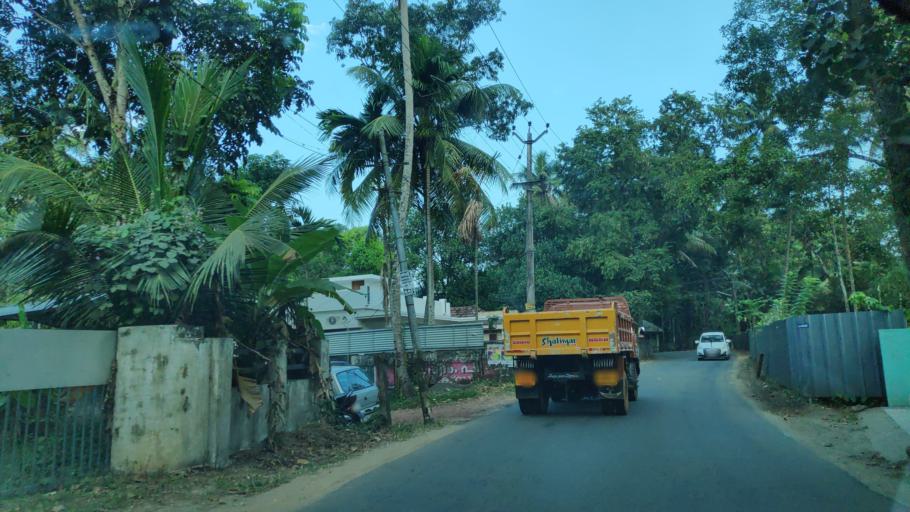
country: IN
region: Kerala
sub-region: Alappuzha
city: Shertallai
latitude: 9.6668
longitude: 76.3878
